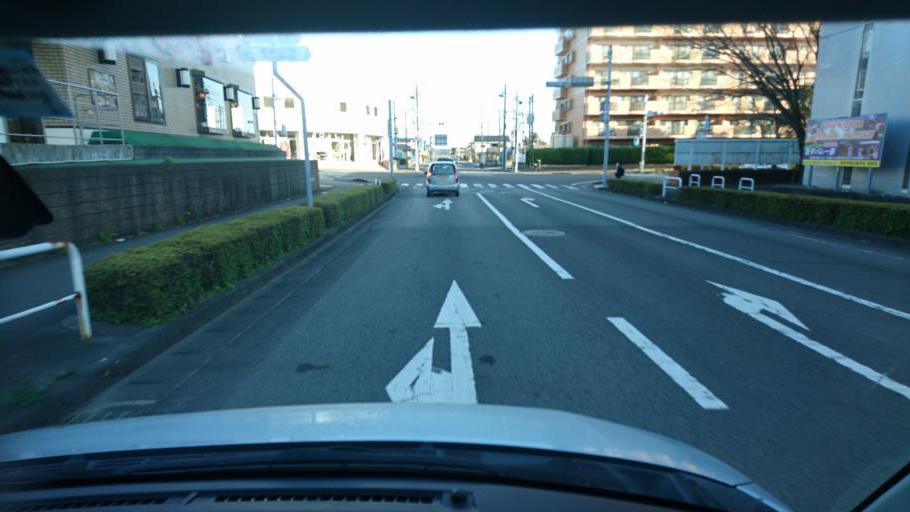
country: JP
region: Miyazaki
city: Miyazaki-shi
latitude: 31.8310
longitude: 131.4204
